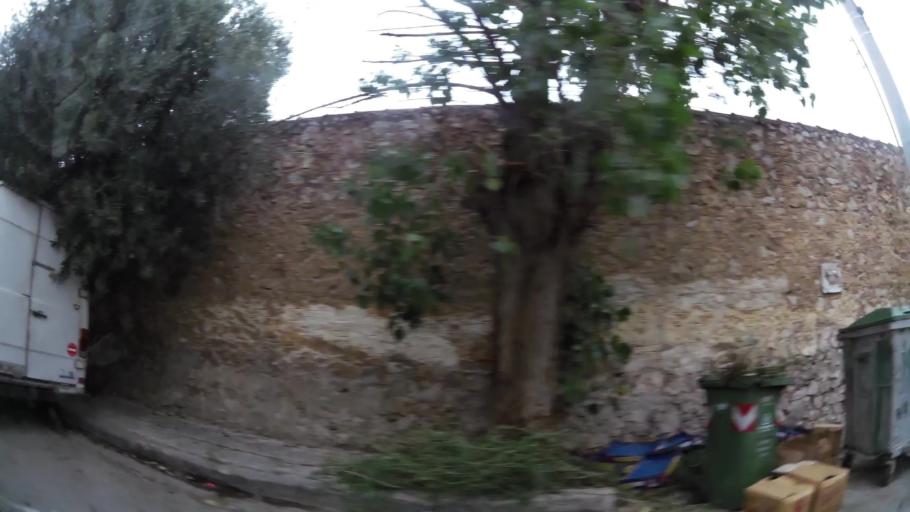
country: GR
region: Attica
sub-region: Nomos Piraios
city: Agios Ioannis Rentis
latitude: 37.9558
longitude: 23.6651
